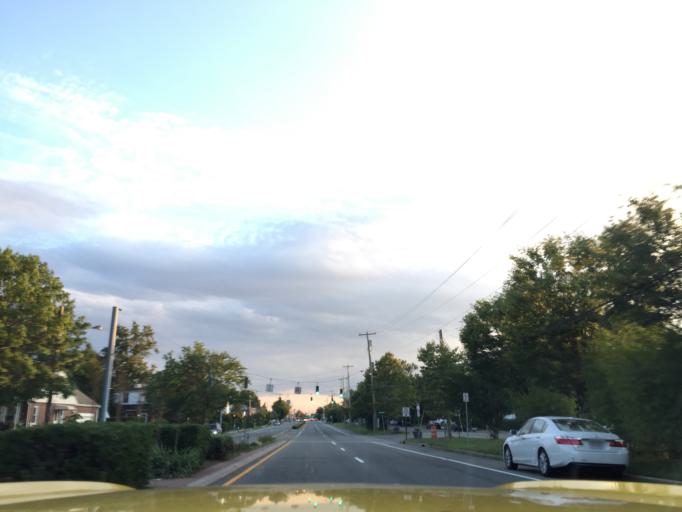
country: US
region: New York
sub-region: Nassau County
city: North New Hyde Park
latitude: 40.7460
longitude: -73.6889
